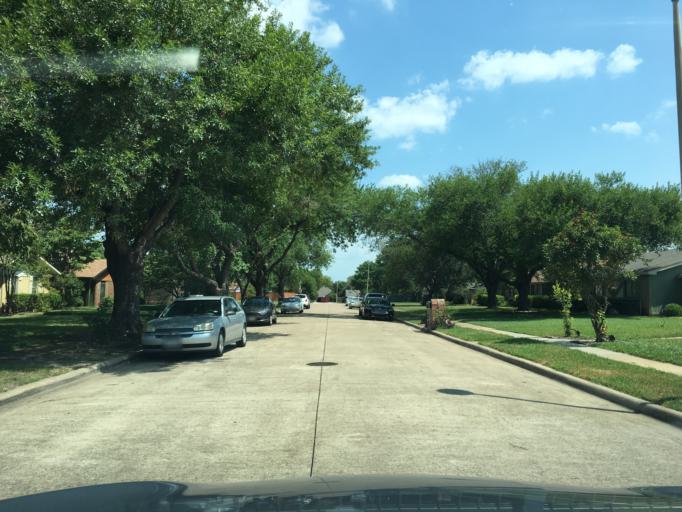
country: US
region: Texas
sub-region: Dallas County
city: Garland
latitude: 32.9643
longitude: -96.6693
